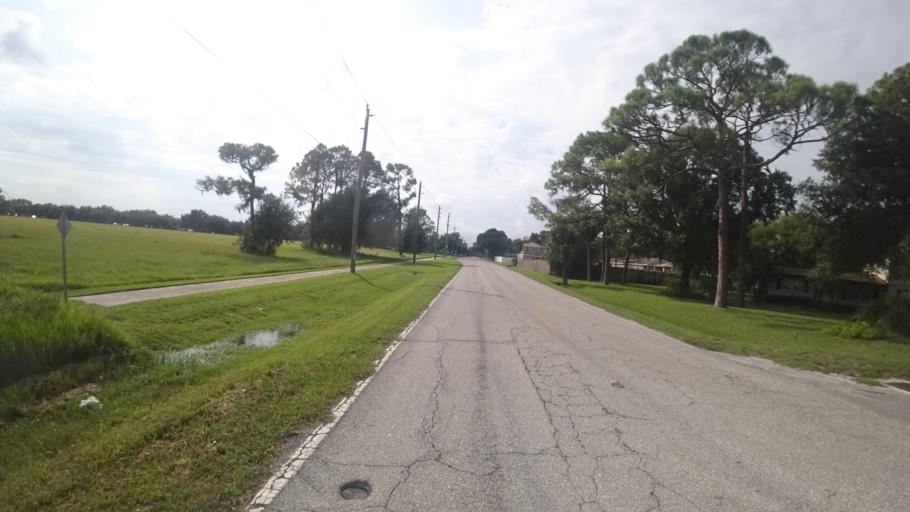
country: US
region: Florida
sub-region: Manatee County
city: Samoset
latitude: 27.4657
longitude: -82.5385
